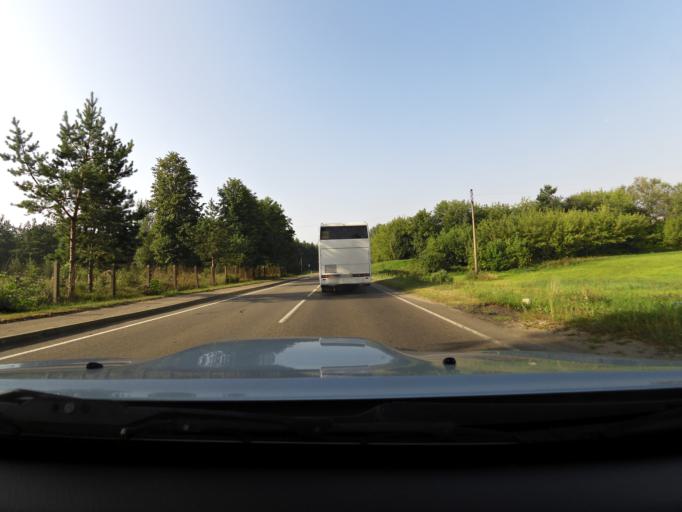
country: LT
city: Lazdijai
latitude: 54.2187
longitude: 23.5054
